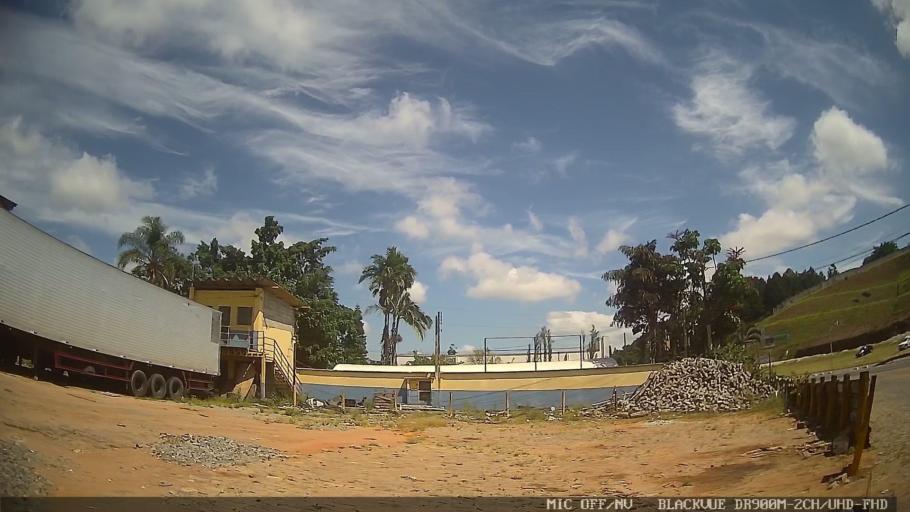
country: BR
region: Sao Paulo
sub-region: Braganca Paulista
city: Braganca Paulista
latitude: -22.9926
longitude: -46.5581
